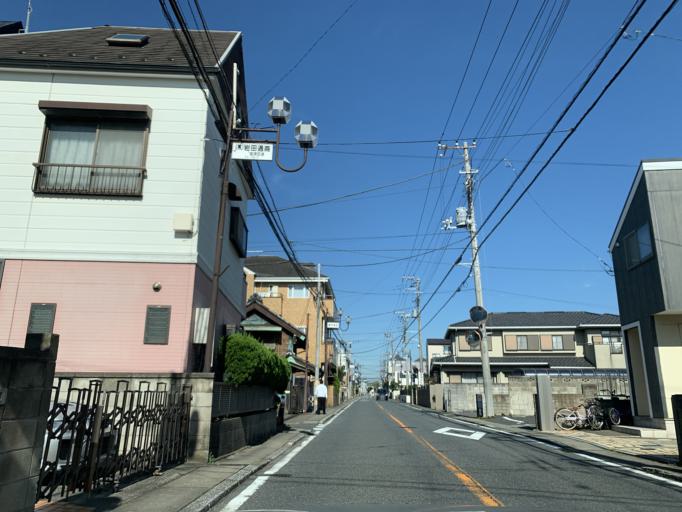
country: JP
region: Tokyo
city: Urayasu
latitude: 35.6928
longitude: 139.9174
